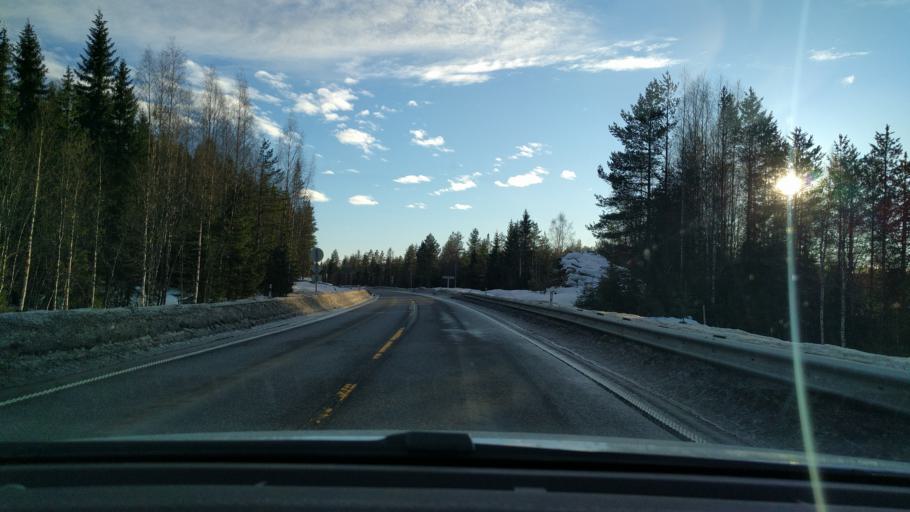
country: NO
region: Hedmark
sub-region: Elverum
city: Elverum
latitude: 61.0451
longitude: 11.8764
